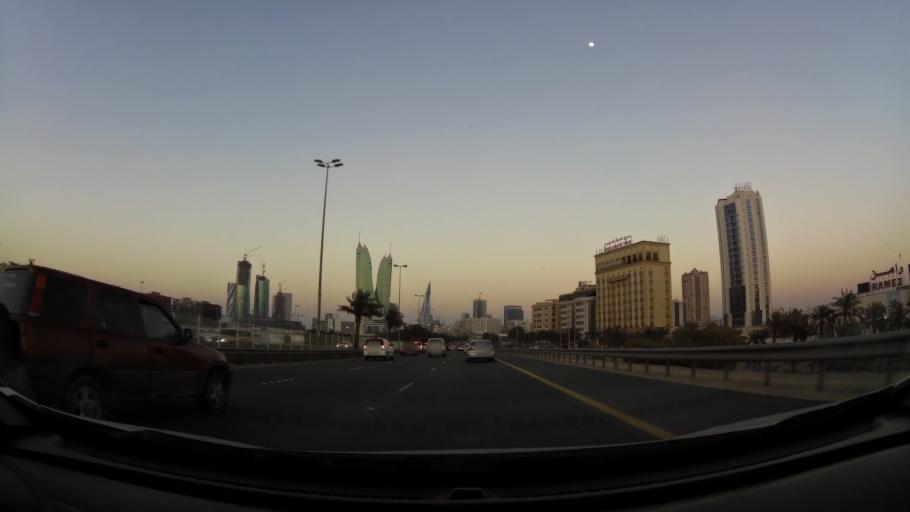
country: BH
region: Manama
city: Jidd Hafs
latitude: 26.2323
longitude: 50.5633
